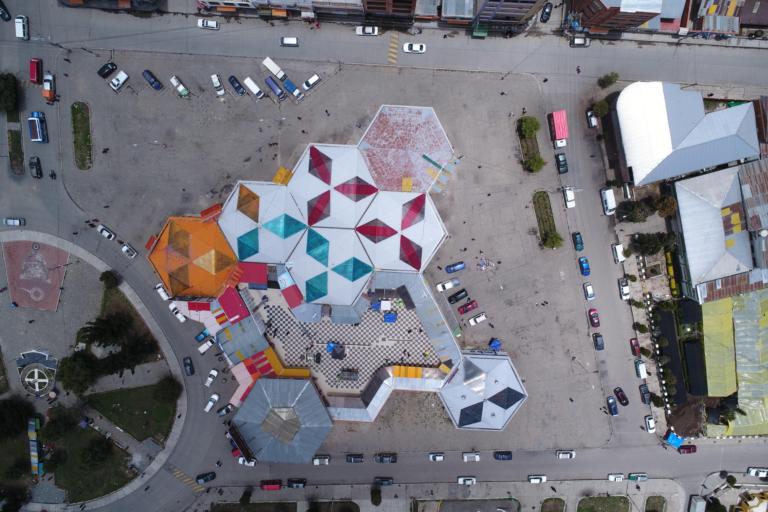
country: BO
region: La Paz
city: La Paz
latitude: -16.5249
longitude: -68.1505
